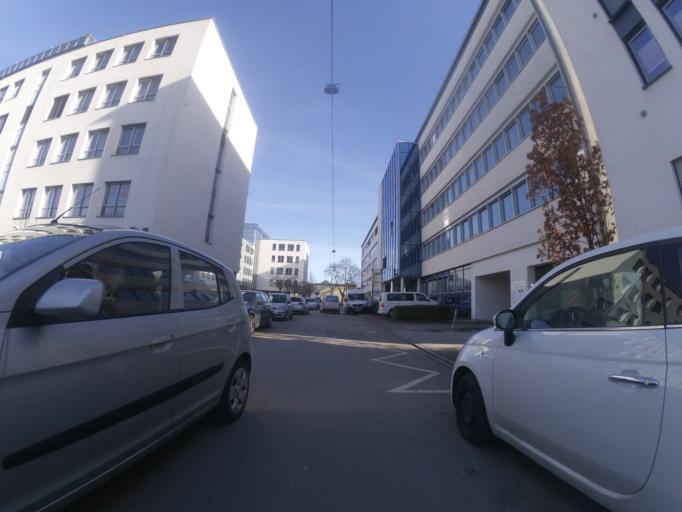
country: DE
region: Baden-Wuerttemberg
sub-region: Tuebingen Region
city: Ulm
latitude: 48.4054
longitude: 9.9880
